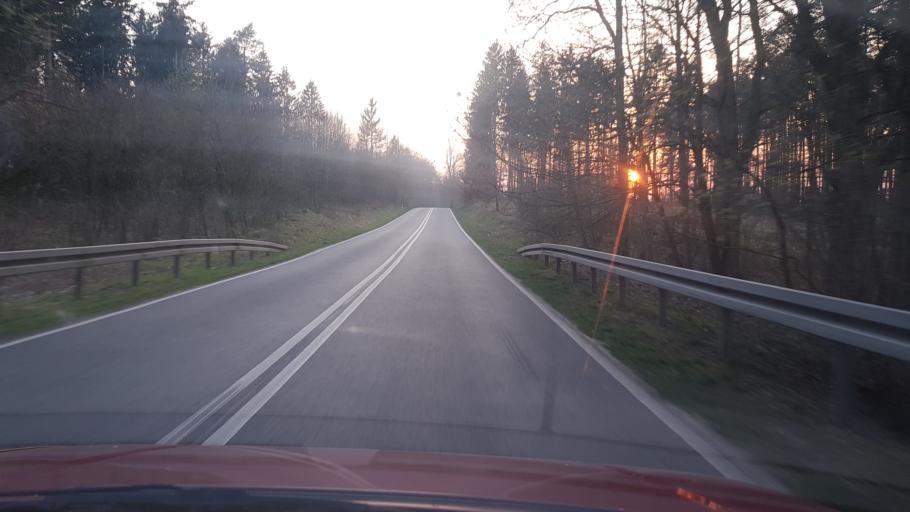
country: PL
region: West Pomeranian Voivodeship
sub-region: Powiat lobeski
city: Radowo Male
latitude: 53.6823
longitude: 15.4051
